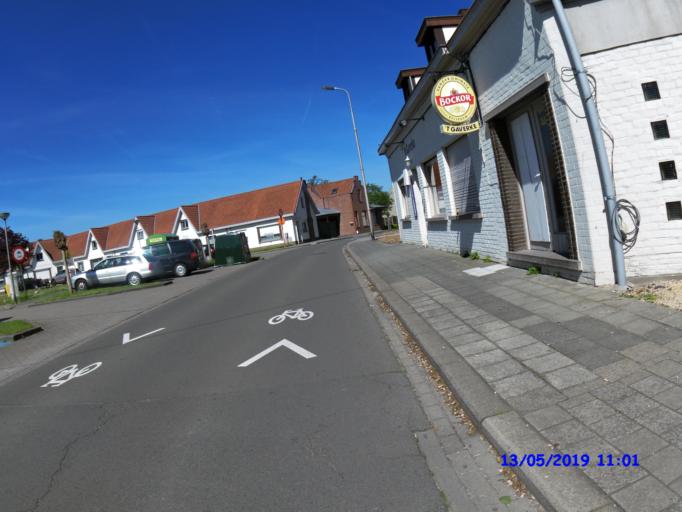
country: BE
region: Flanders
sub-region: Provincie West-Vlaanderen
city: Waregem
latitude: 50.8869
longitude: 3.4176
